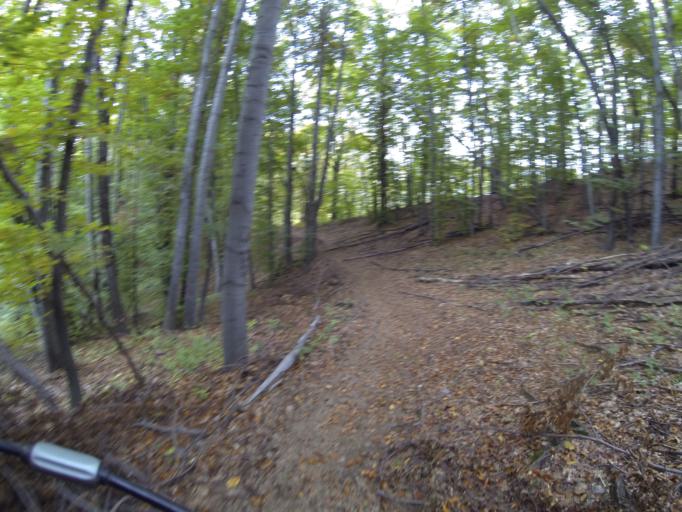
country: RO
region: Gorj
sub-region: Comuna Tismana
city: Sohodol
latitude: 45.0918
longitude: 22.8861
